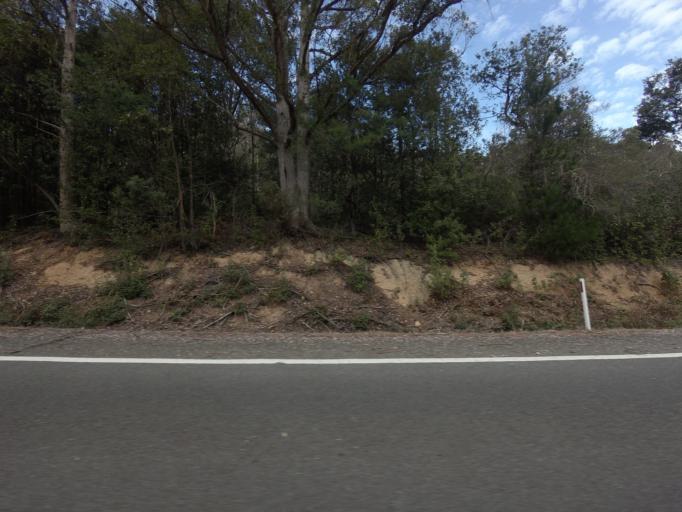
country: AU
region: Tasmania
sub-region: Meander Valley
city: Deloraine
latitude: -41.6465
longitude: 146.7193
